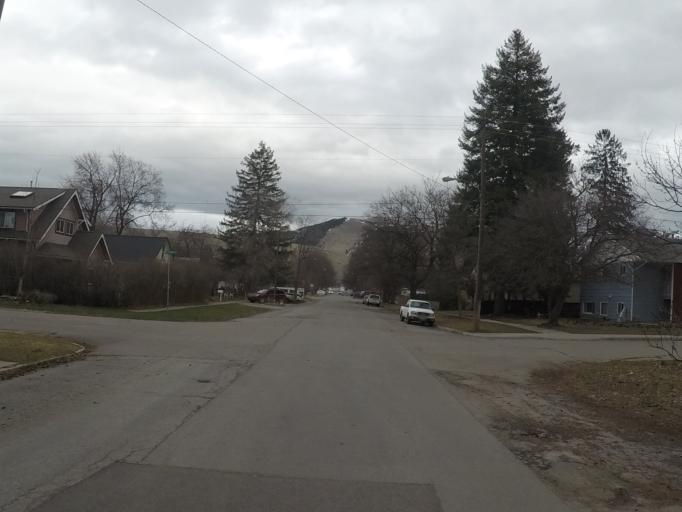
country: US
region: Montana
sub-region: Missoula County
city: Missoula
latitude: 46.8790
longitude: -114.0081
